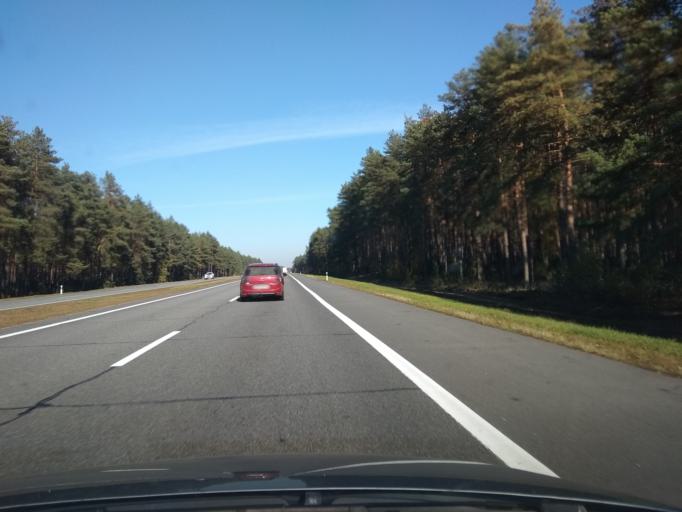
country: BY
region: Brest
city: Baranovichi
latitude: 52.9799
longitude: 25.7459
